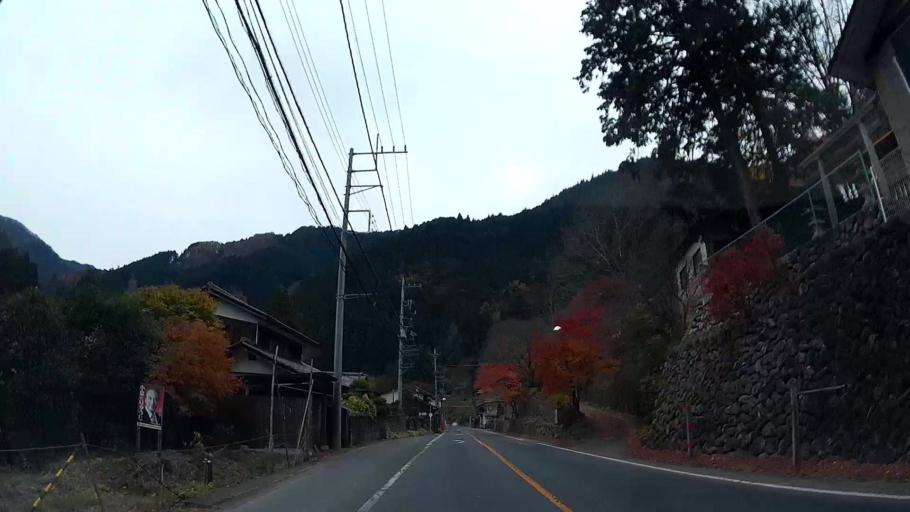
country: JP
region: Saitama
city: Chichibu
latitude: 35.9533
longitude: 138.9639
